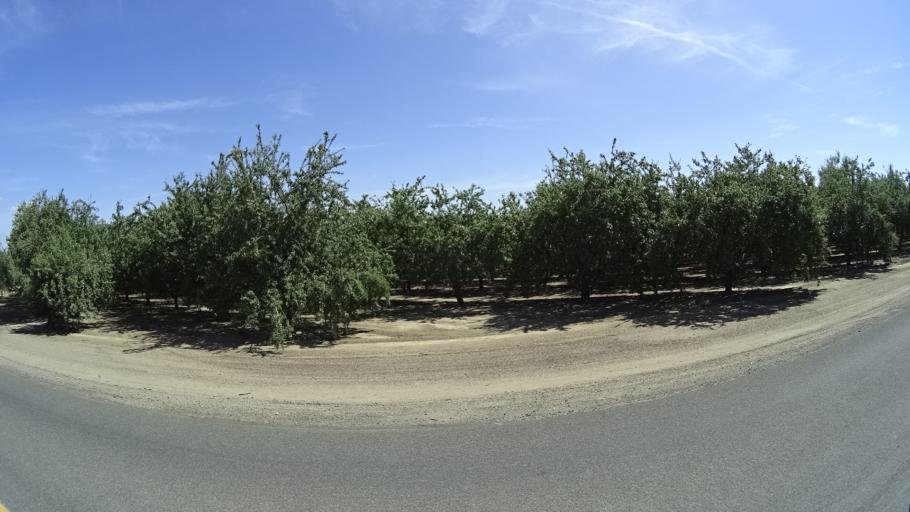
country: US
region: California
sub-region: Kings County
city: Kettleman City
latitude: 35.9775
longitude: -119.9475
